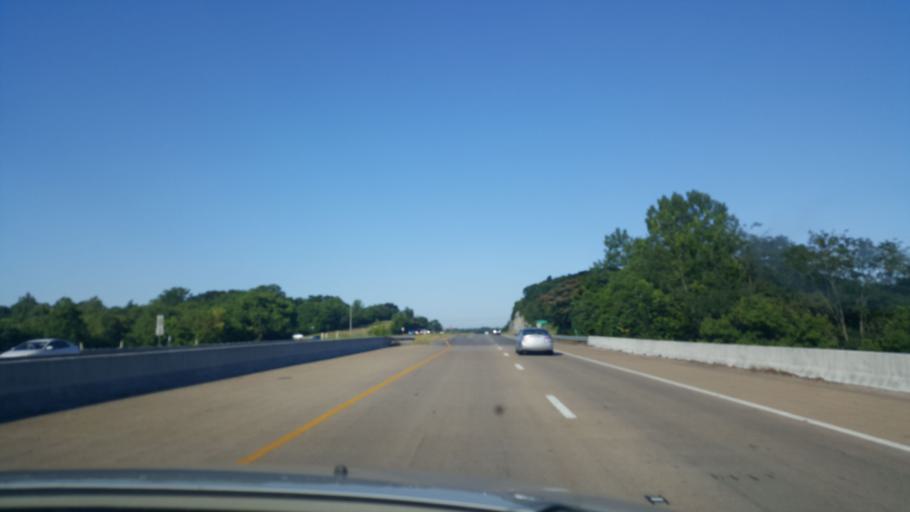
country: US
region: Tennessee
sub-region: Maury County
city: Columbia
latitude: 35.6292
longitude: -87.1038
